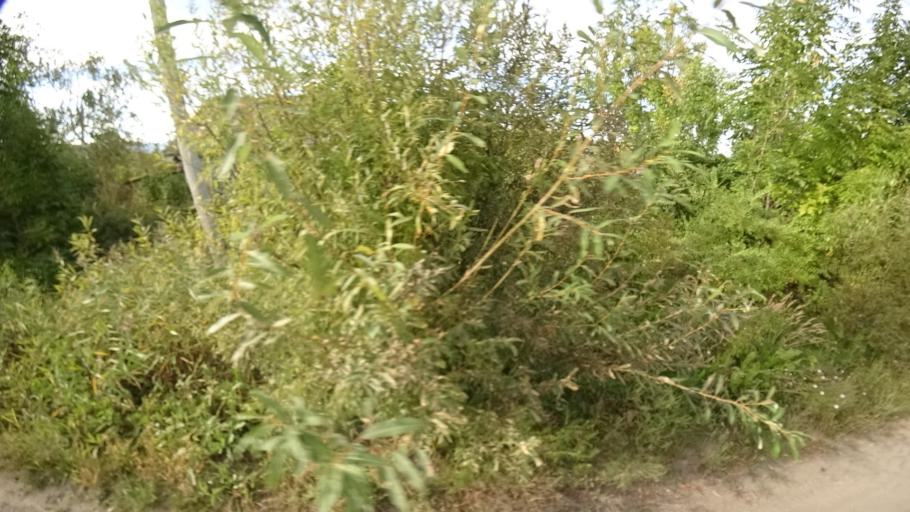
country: RU
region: Primorskiy
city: Dostoyevka
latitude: 44.2901
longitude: 133.4291
